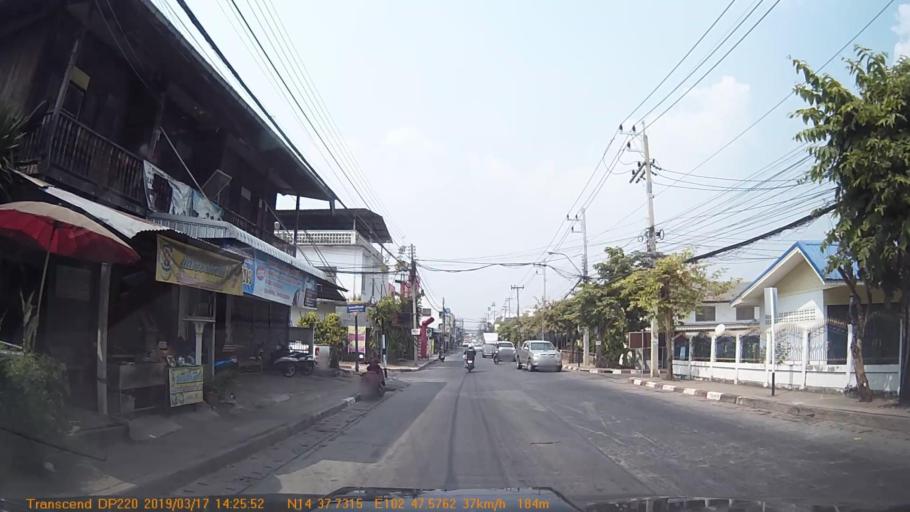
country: TH
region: Buriram
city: Nang Rong
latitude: 14.6290
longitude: 102.7930
